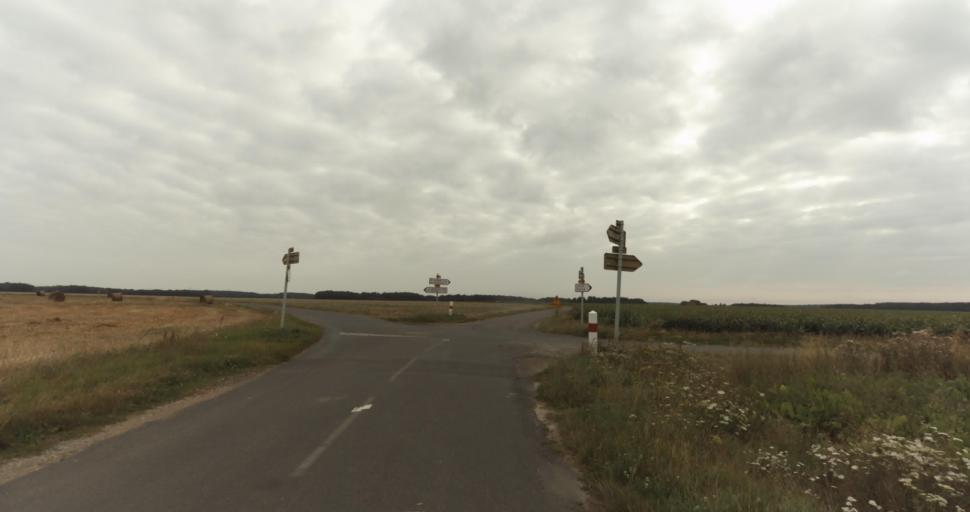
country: FR
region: Haute-Normandie
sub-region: Departement de l'Eure
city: Marcilly-sur-Eure
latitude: 48.8204
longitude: 1.2899
